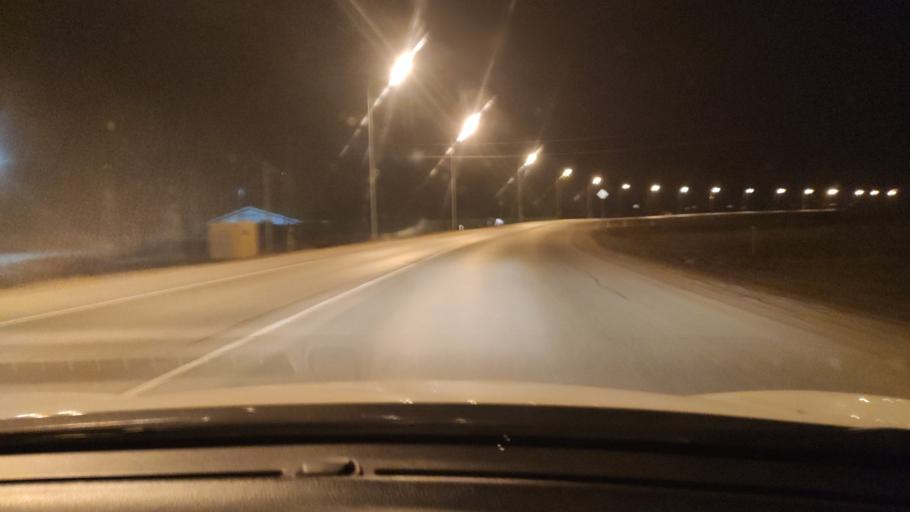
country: RU
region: Tatarstan
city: Laishevo
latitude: 55.4274
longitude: 49.7127
